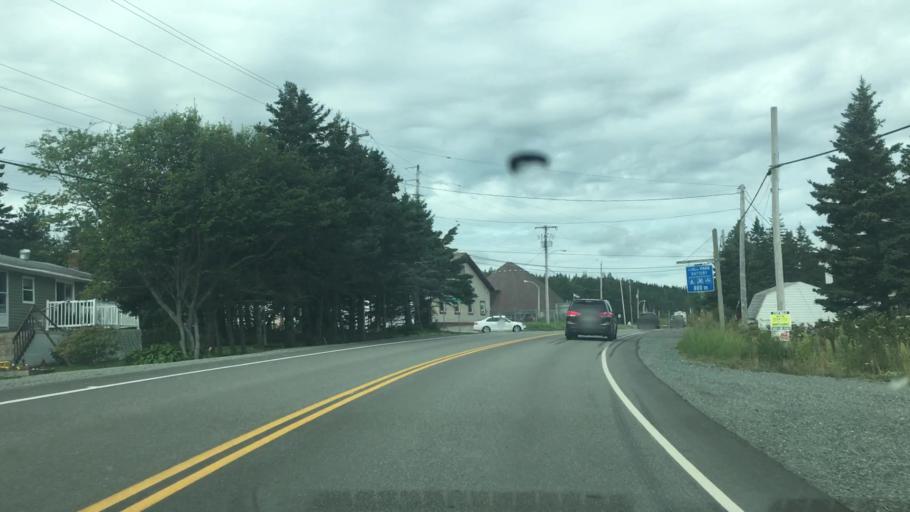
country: CA
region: Nova Scotia
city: Princeville
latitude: 45.6516
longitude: -60.8567
